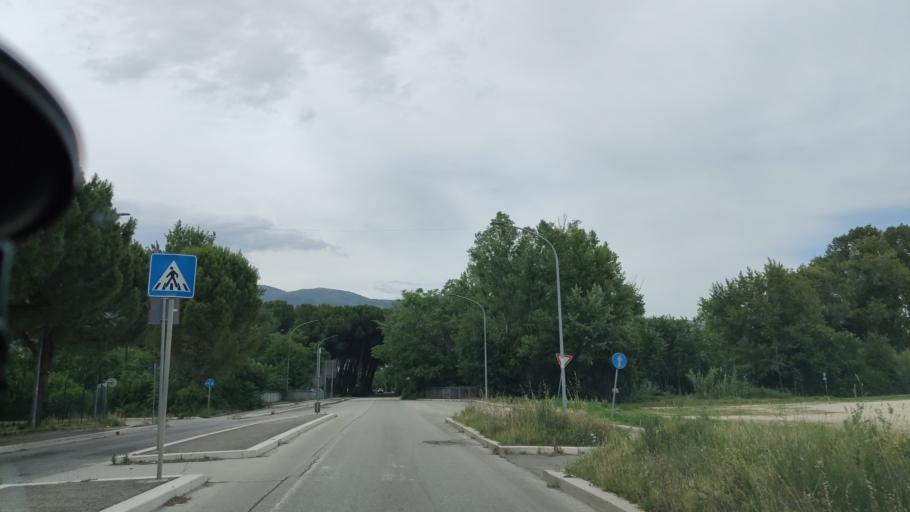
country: IT
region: Umbria
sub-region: Provincia di Terni
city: Terni
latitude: 42.5603
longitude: 12.6575
